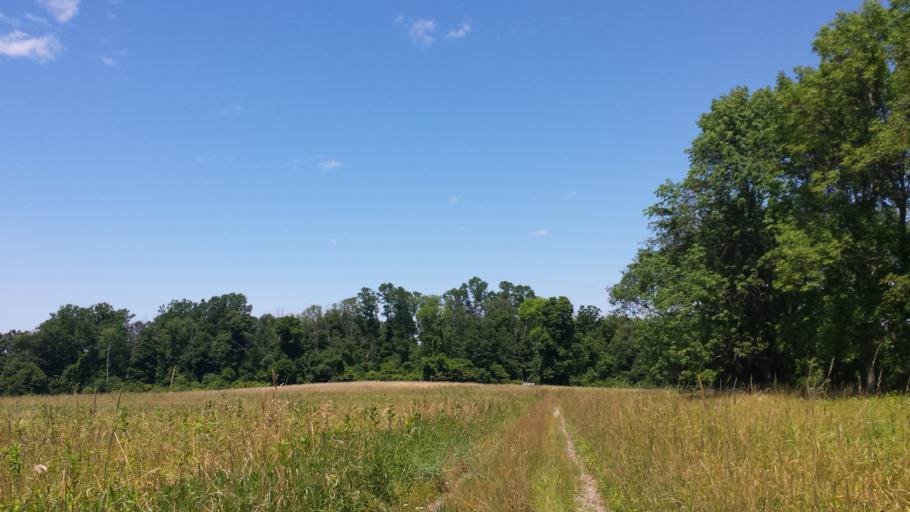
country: US
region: New York
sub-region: Westchester County
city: Mount Kisco
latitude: 41.1804
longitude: -73.7015
